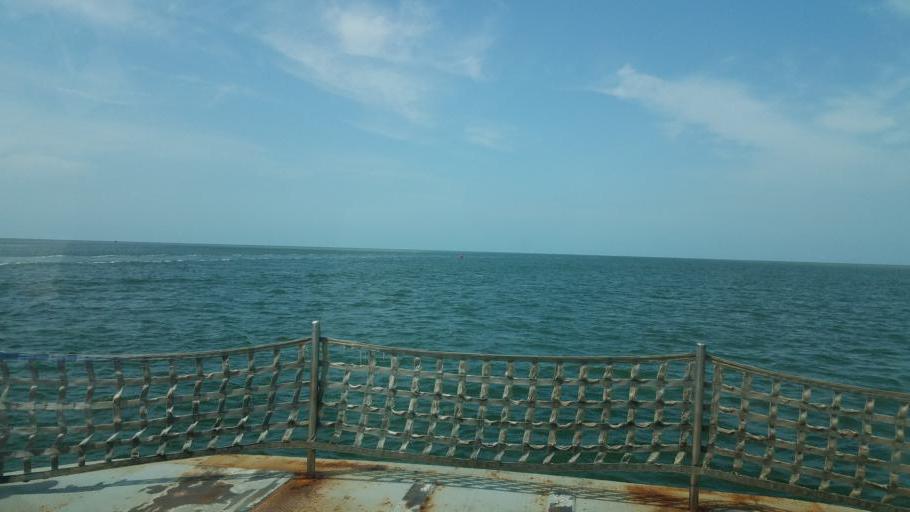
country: US
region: North Carolina
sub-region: Dare County
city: Buxton
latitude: 35.1981
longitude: -75.7830
